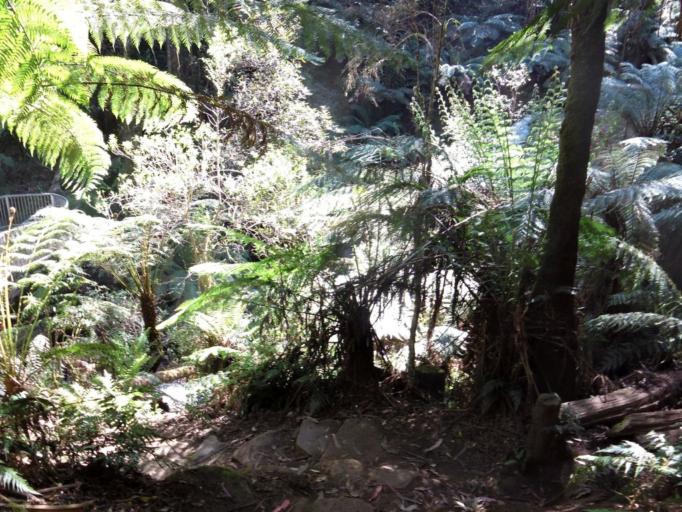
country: AU
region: Victoria
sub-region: Baw Baw
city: Warragul
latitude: -37.8435
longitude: 146.0483
